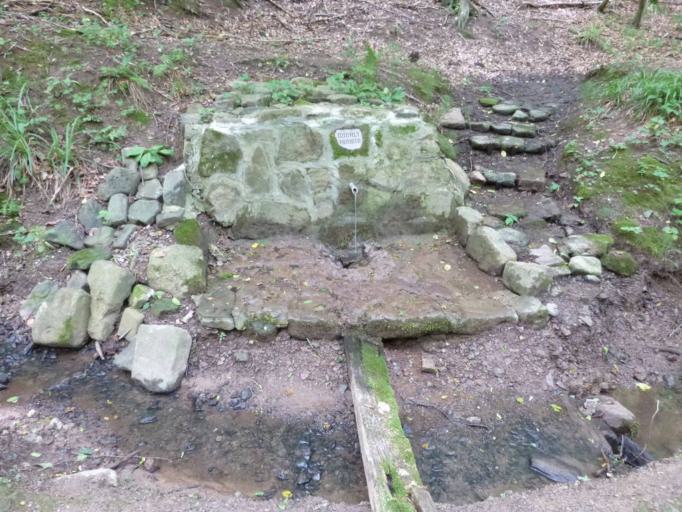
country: HU
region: Baranya
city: Pellerd
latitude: 46.1050
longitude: 18.1551
